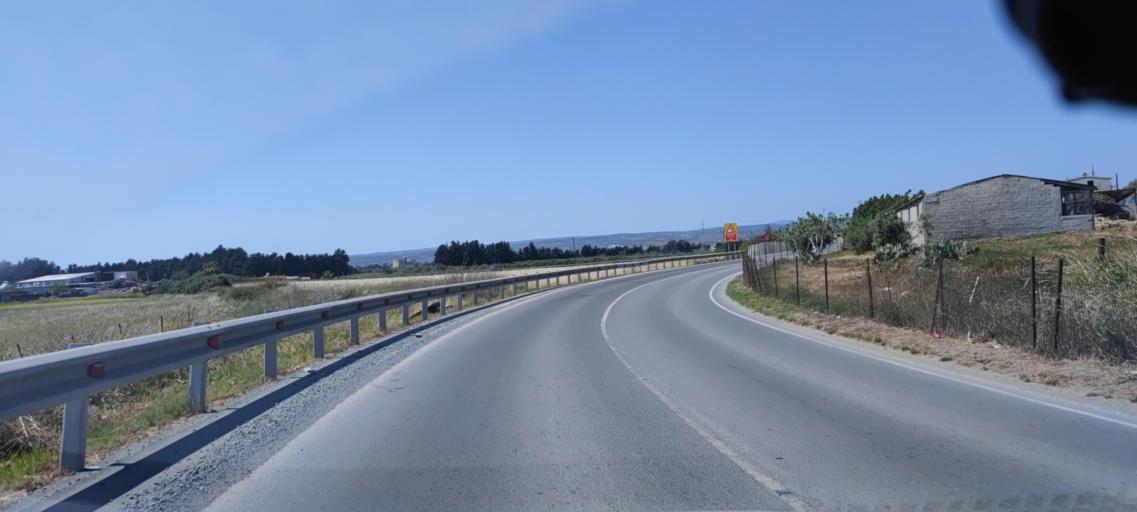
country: CY
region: Larnaka
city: Kolossi
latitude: 34.6546
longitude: 32.9500
